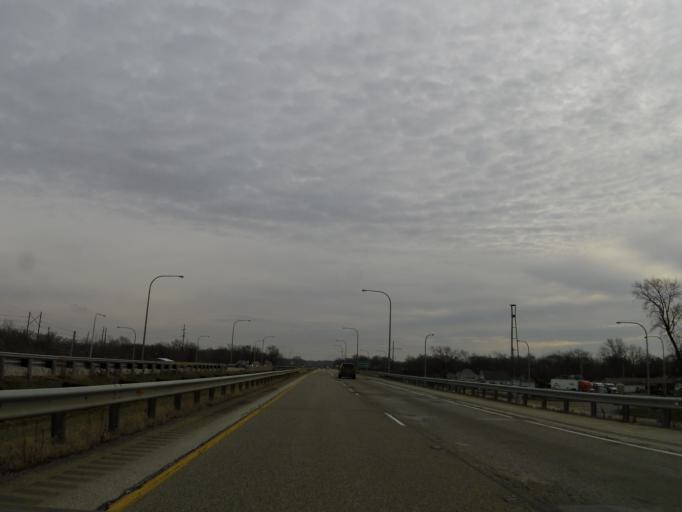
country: US
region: Illinois
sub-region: Vermilion County
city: Tilton
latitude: 40.1051
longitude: -87.6506
